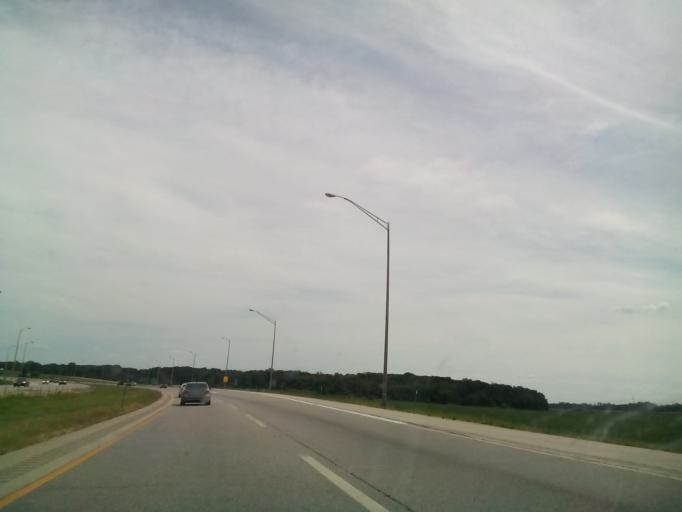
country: US
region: Illinois
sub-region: Kane County
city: Sugar Grove
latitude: 41.8208
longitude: -88.4735
